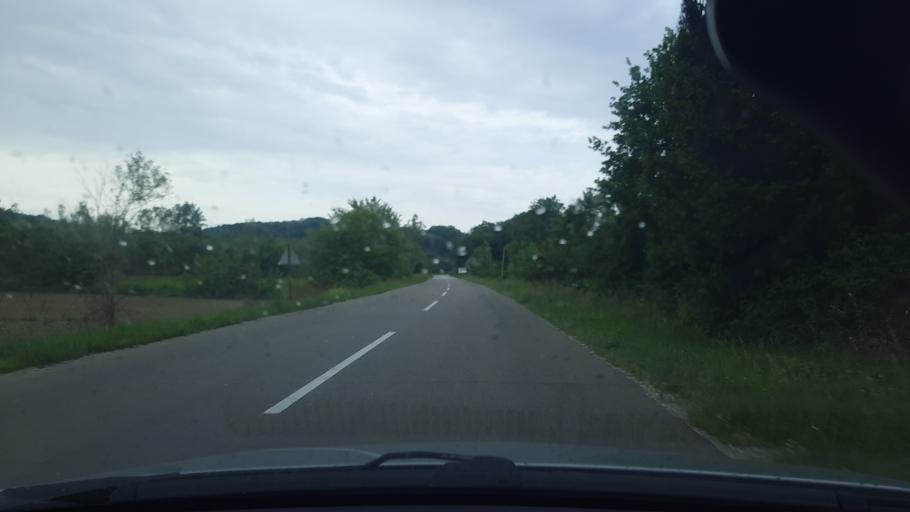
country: RS
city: Jarebice
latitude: 44.4868
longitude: 19.4839
